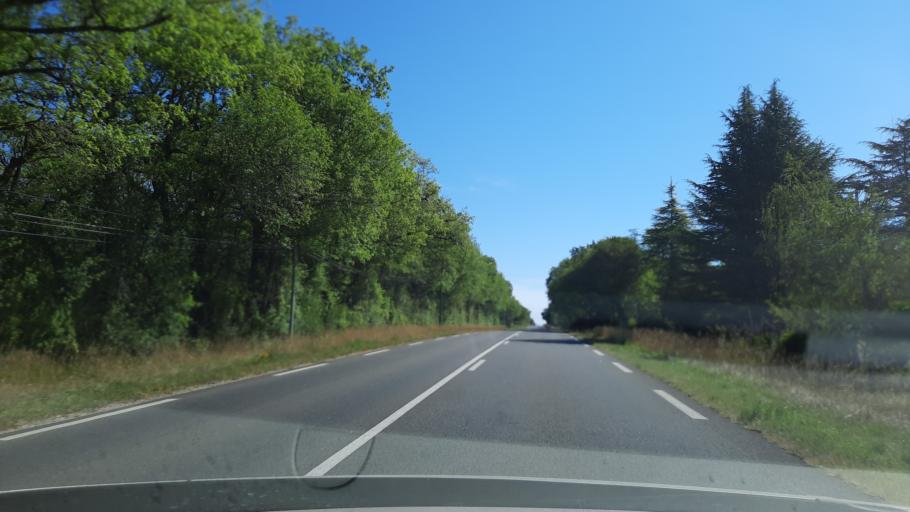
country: FR
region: Midi-Pyrenees
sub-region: Departement du Tarn-et-Garonne
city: Caylus
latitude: 44.2142
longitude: 1.7296
